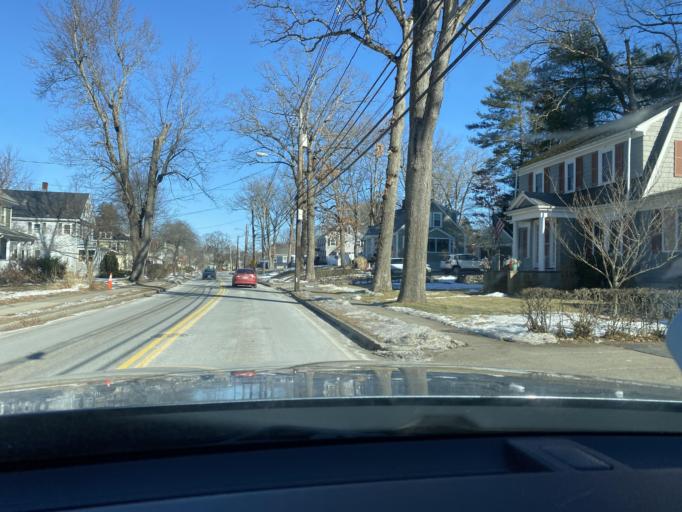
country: US
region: Massachusetts
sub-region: Norfolk County
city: Walpole
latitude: 42.1544
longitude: -71.2141
